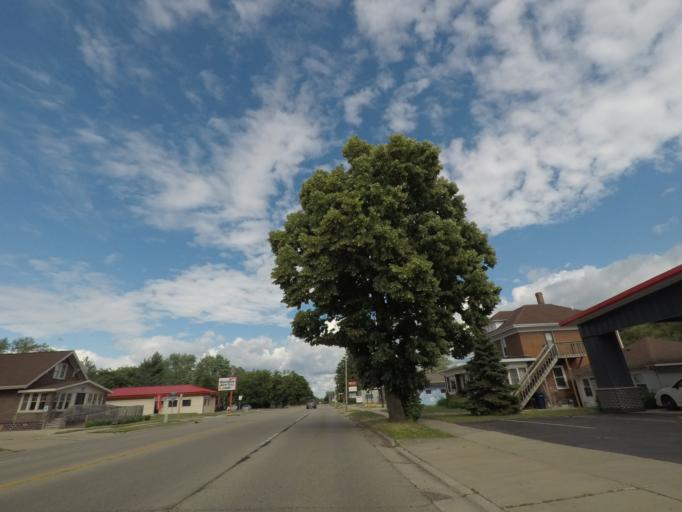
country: US
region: Wisconsin
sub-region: Rock County
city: Janesville
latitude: 42.6793
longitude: -89.0413
